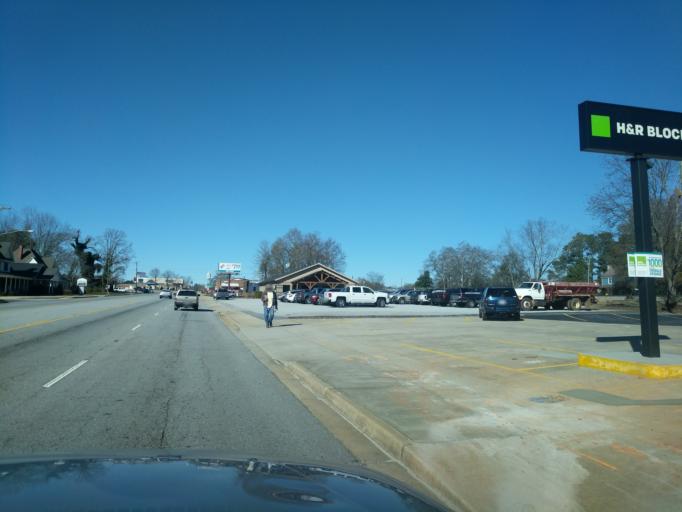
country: US
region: South Carolina
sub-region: Oconee County
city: Westminster
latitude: 34.6617
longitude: -83.0917
